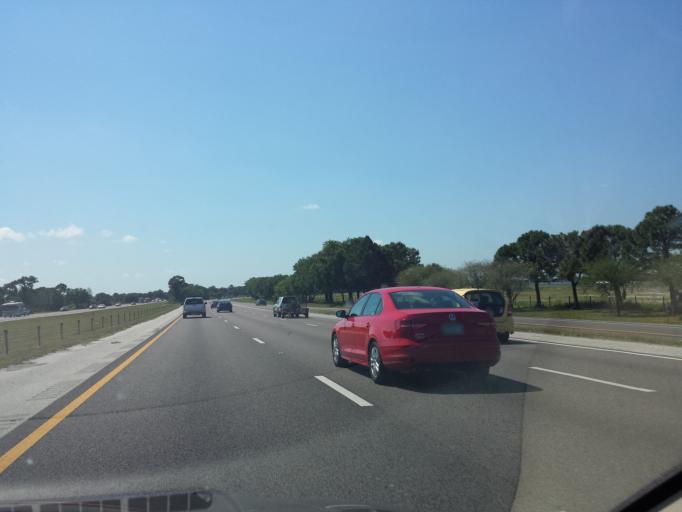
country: US
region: Florida
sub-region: Sarasota County
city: The Meadows
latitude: 27.3853
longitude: -82.4480
